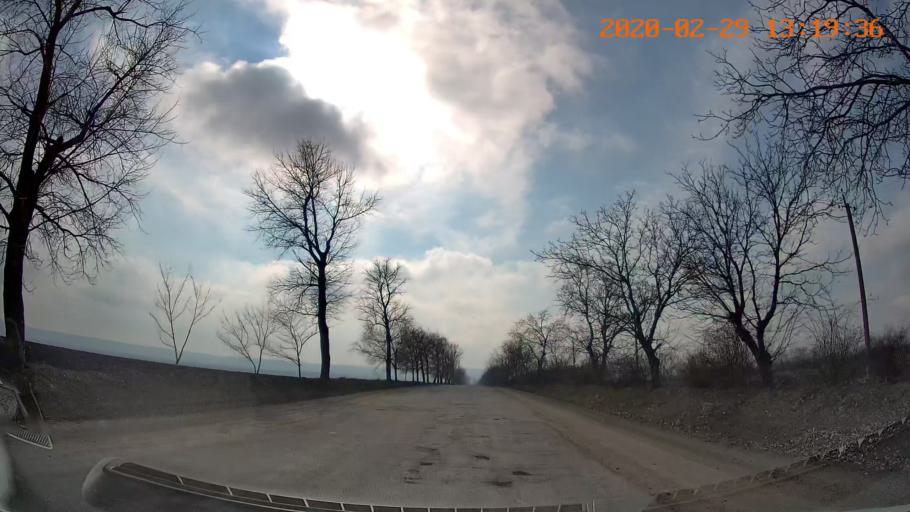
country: MD
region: Telenesti
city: Camenca
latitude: 47.9871
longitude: 28.6495
